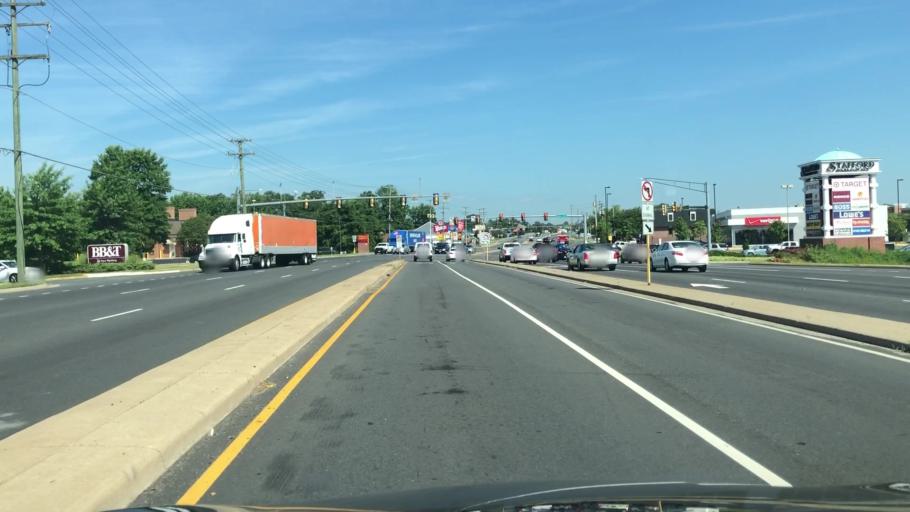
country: US
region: Virginia
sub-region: Stafford County
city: Aquia Harbour
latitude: 38.4679
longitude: -77.4112
